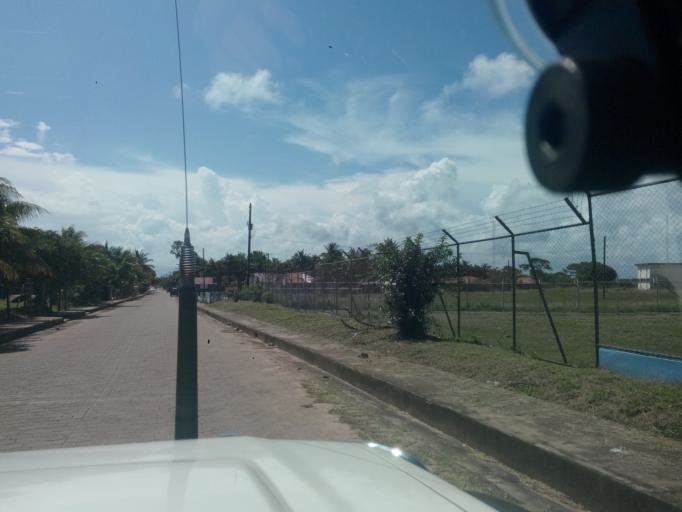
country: NI
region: Atlantico Norte (RAAN)
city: Puerto Cabezas
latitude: 14.0417
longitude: -83.3811
